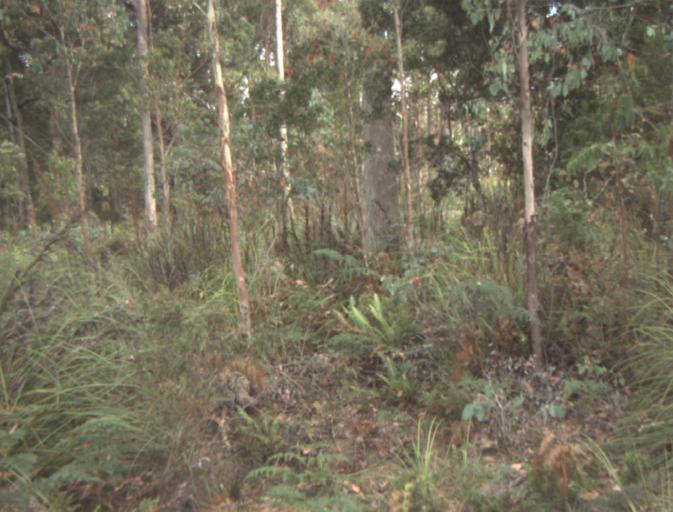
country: AU
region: Tasmania
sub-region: Launceston
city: Mayfield
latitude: -41.2913
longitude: 147.2402
